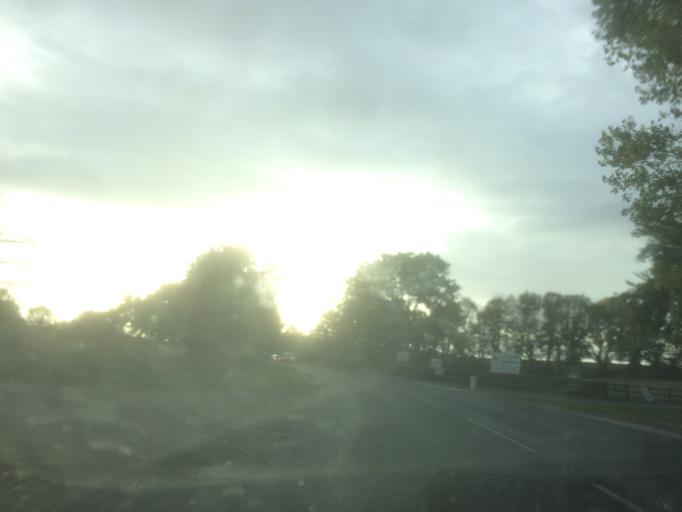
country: GB
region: England
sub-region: City and Borough of Wakefield
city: Ferrybridge
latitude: 53.7163
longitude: -1.2924
